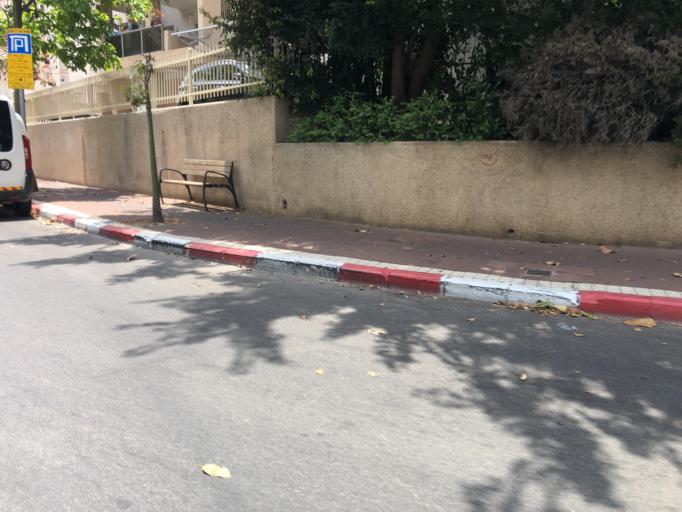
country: IL
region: Tel Aviv
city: Bene Beraq
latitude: 32.0635
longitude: 34.8328
